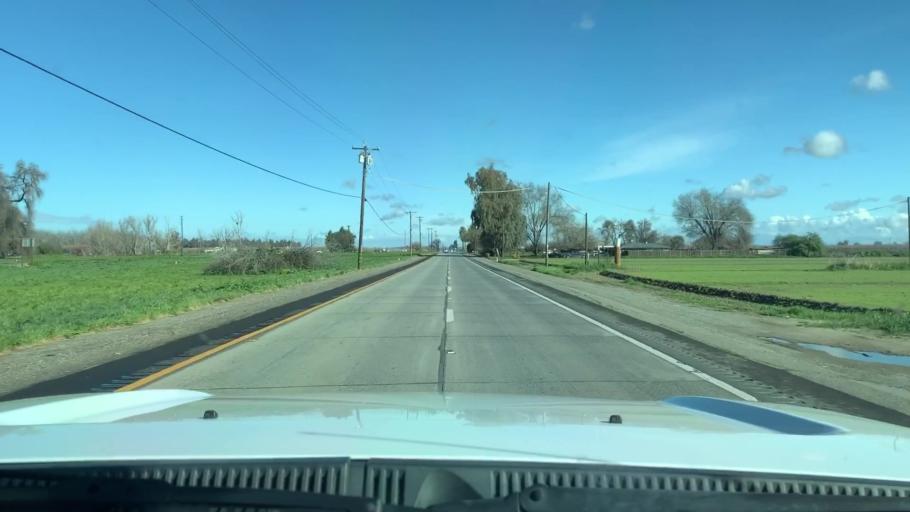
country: US
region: California
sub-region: Kings County
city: Lemoore
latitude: 36.3664
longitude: -119.8097
